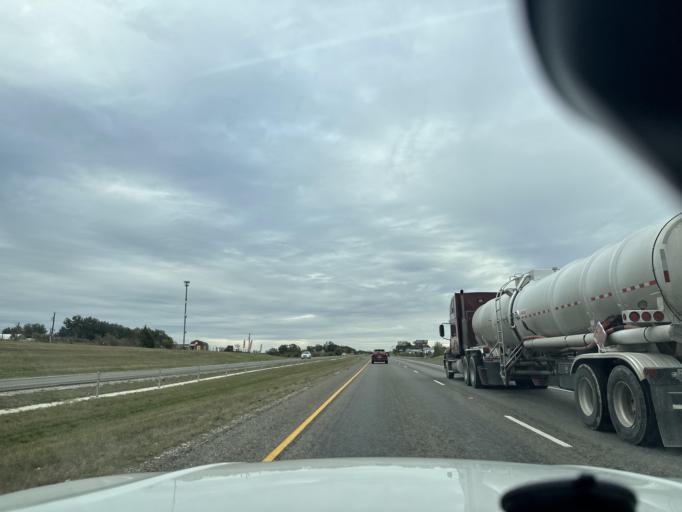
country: US
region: Texas
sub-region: Burleson County
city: Somerville
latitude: 30.1858
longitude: -96.5739
